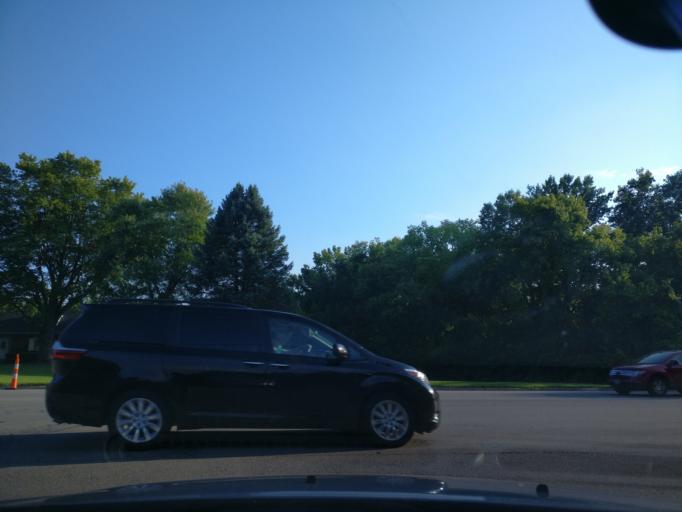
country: US
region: Ohio
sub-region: Warren County
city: Springboro
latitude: 39.5579
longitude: -84.2365
